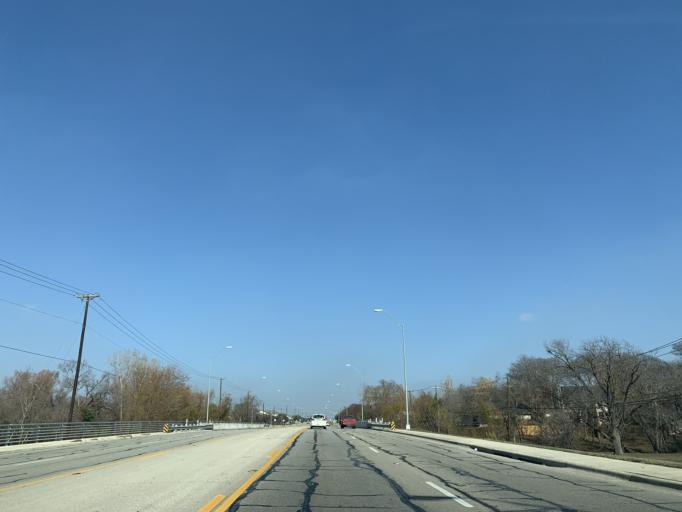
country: US
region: Texas
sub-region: Williamson County
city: Round Rock
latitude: 30.5347
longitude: -97.6520
